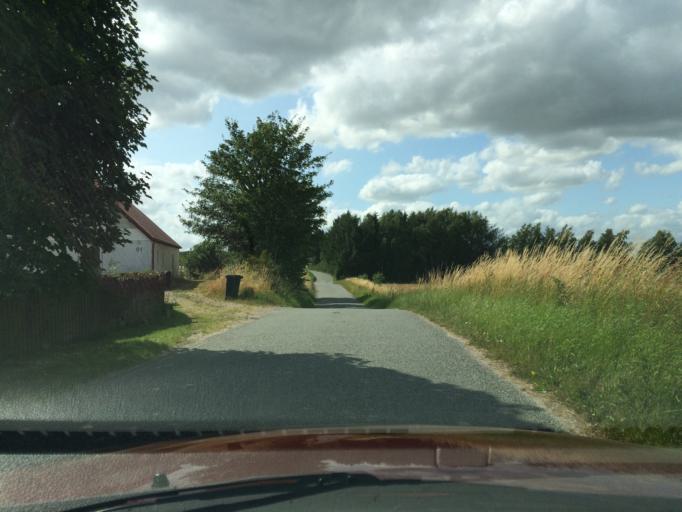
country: DK
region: Central Jutland
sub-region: Skanderborg Kommune
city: Galten
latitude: 56.1575
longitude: 9.8729
